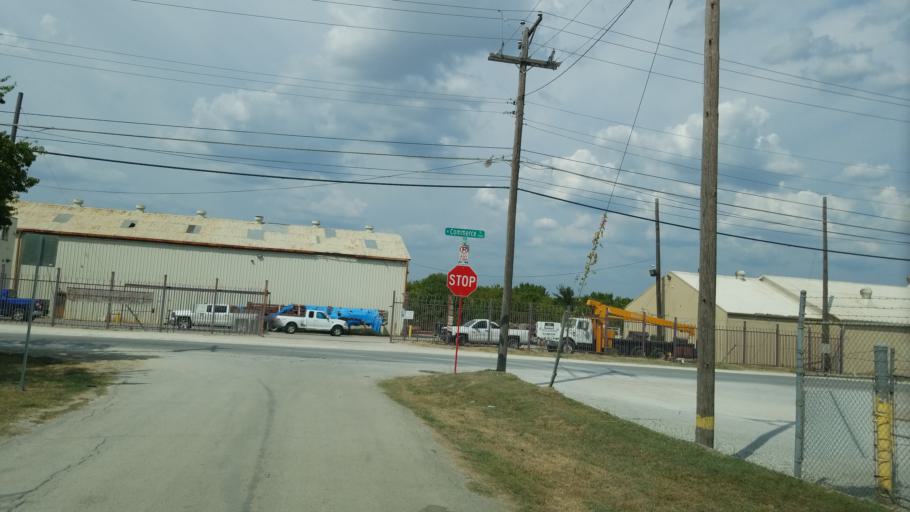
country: US
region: Texas
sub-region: Dallas County
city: Dallas
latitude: 32.7718
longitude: -96.8456
